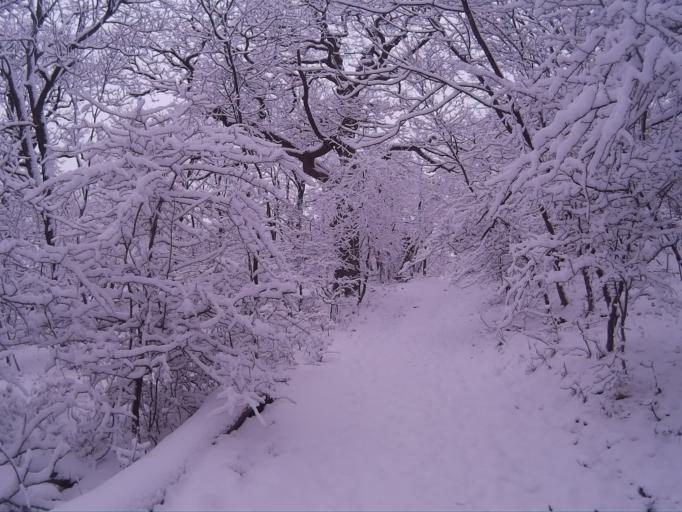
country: HU
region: Komarom-Esztergom
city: Tarjan
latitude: 47.5723
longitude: 18.5323
